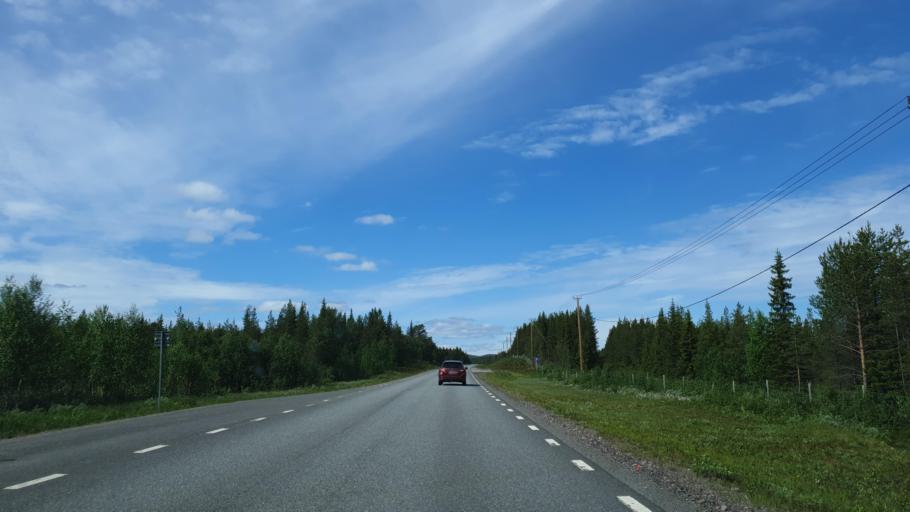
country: SE
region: Vaesterbotten
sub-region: Mala Kommun
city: Mala
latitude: 65.6111
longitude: 18.7163
